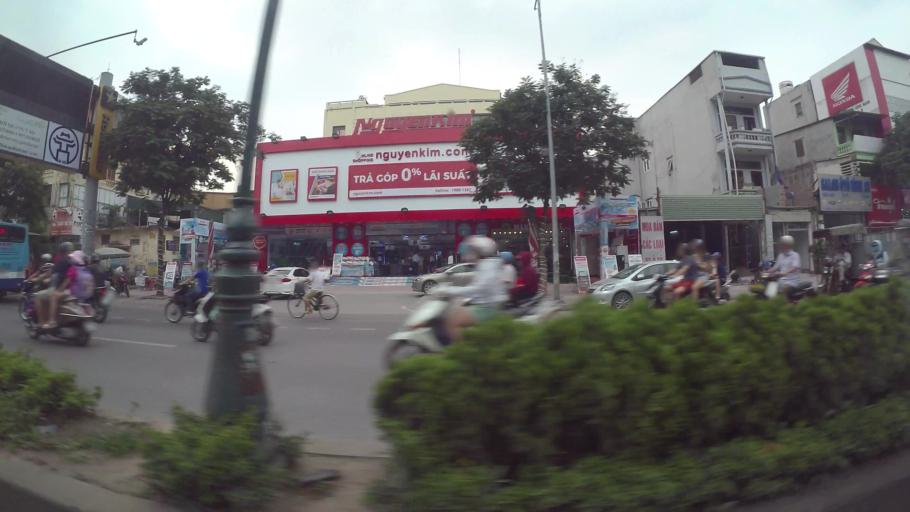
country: VN
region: Ha Noi
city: Hoan Kiem
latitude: 21.0455
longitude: 105.8755
